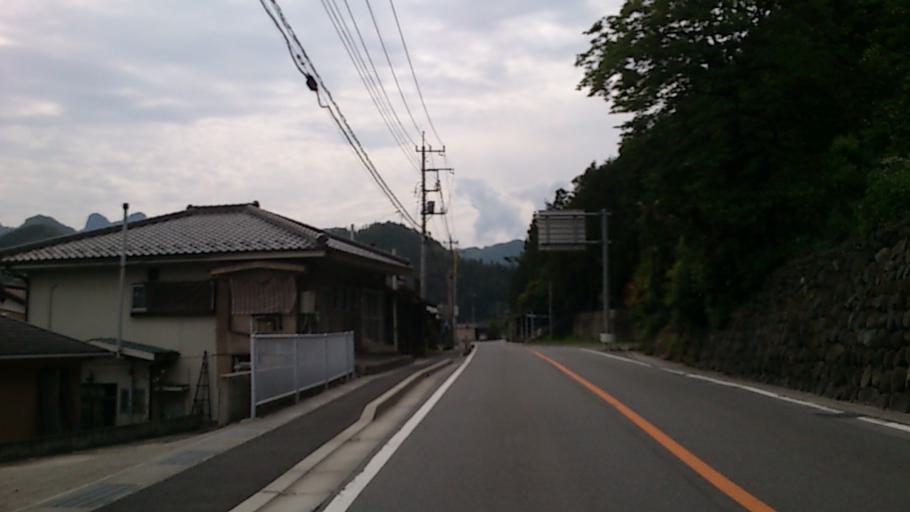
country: JP
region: Gunma
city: Tomioka
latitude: 36.2137
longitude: 138.7844
